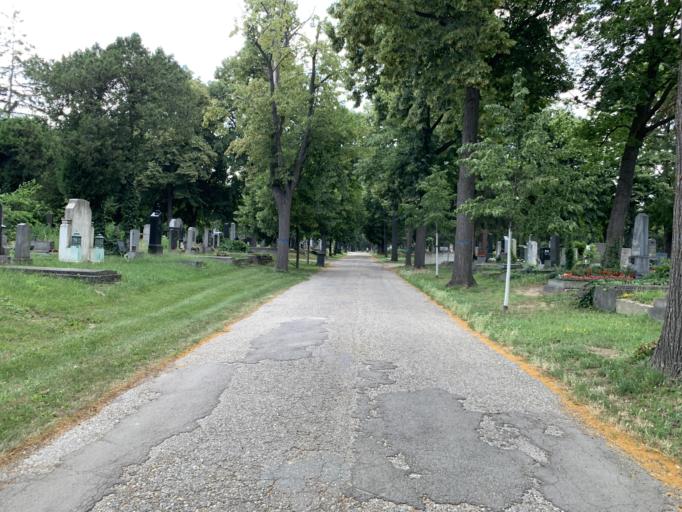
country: AT
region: Lower Austria
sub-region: Politischer Bezirk Wien-Umgebung
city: Schwechat
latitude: 48.1512
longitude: 16.4313
